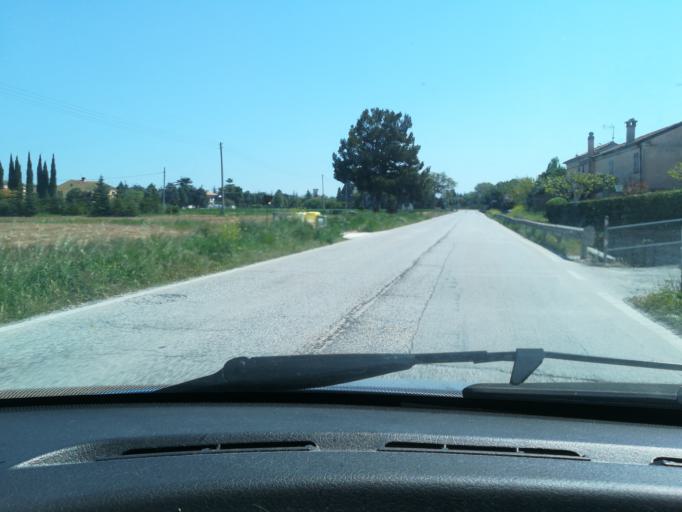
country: IT
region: The Marches
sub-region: Provincia di Ancona
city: Castelfidardo
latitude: 43.4531
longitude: 13.5276
